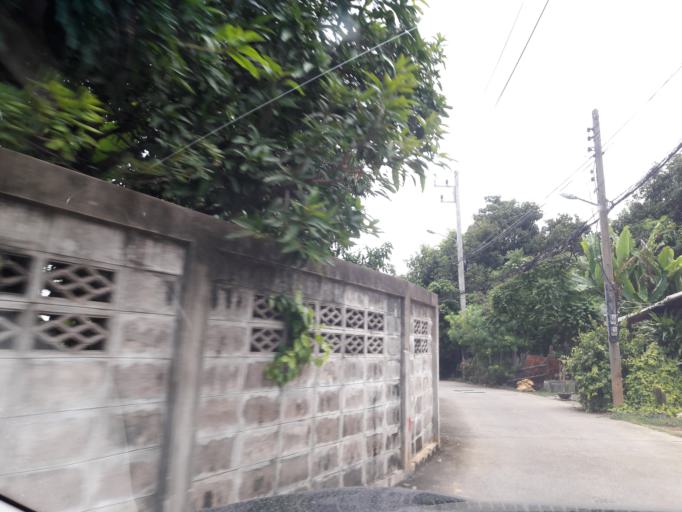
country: TH
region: Ratchaburi
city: Ratchaburi
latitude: 13.5491
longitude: 99.8205
